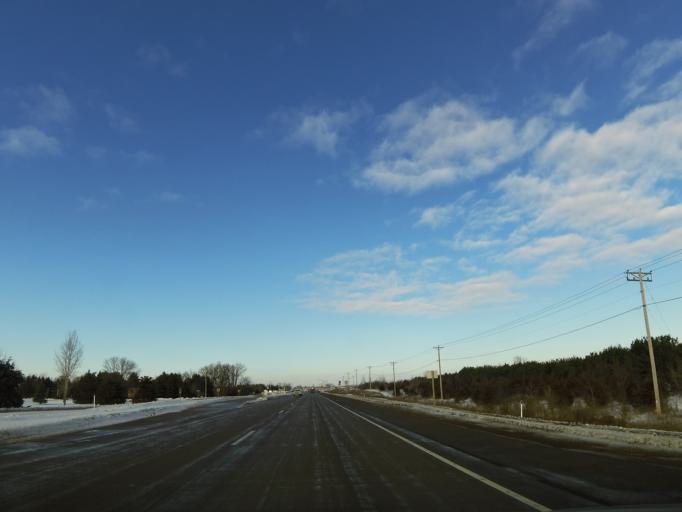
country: US
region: Wisconsin
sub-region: Saint Croix County
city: Hudson
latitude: 44.9732
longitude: -92.6799
